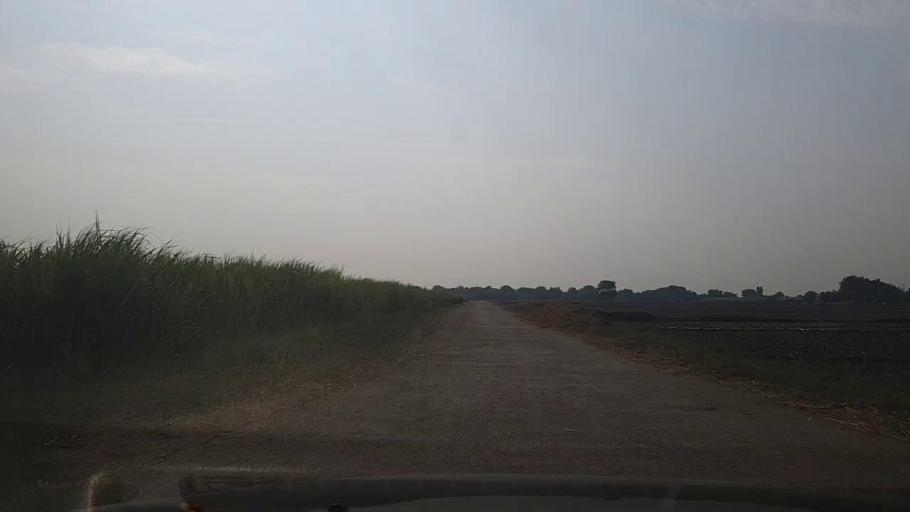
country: PK
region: Sindh
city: Bulri
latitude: 25.0109
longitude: 68.2999
